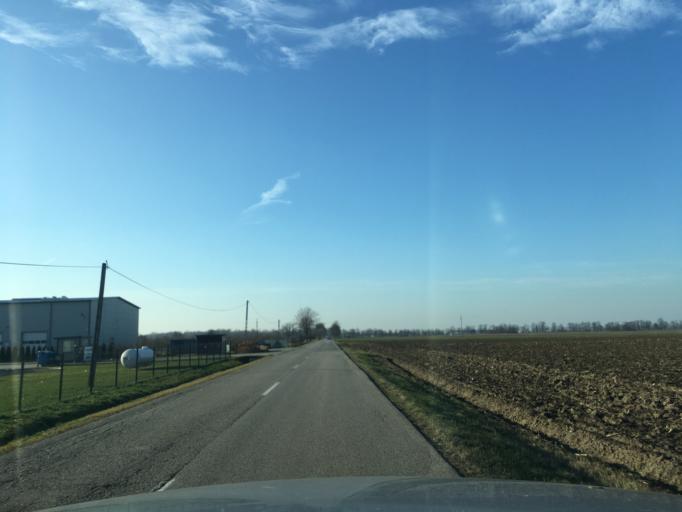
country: PL
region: Masovian Voivodeship
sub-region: Powiat pruszkowski
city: Nadarzyn
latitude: 52.0427
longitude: 20.8067
